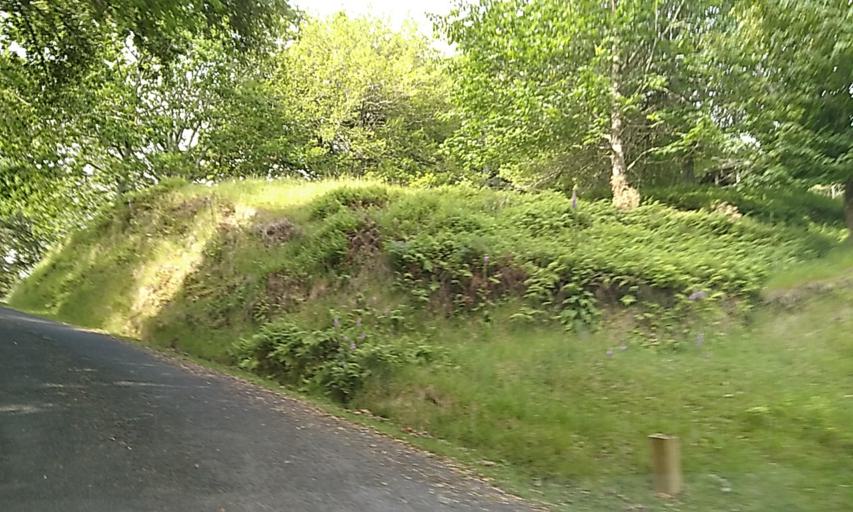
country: NZ
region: Bay of Plenty
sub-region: Tauranga City
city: Tauranga
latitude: -37.8150
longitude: 176.0416
